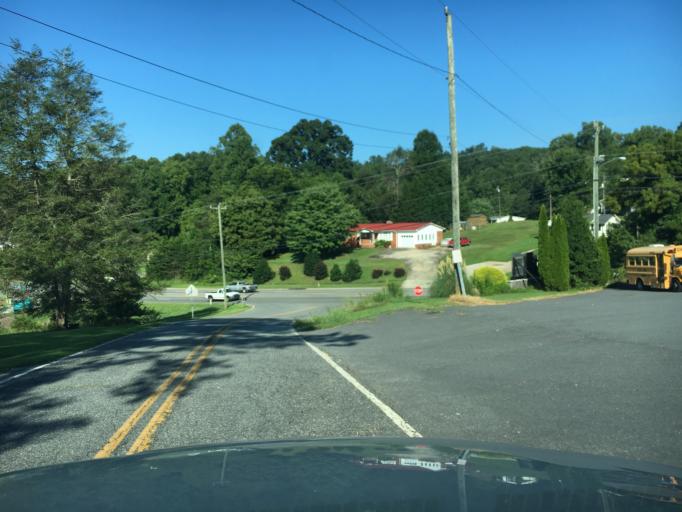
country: US
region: North Carolina
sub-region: McDowell County
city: West Marion
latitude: 35.6557
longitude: -82.0267
